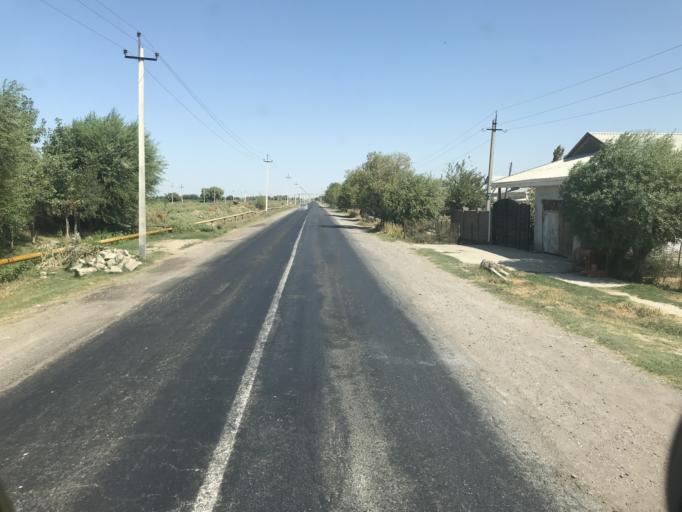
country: KZ
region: Ongtustik Qazaqstan
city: Ilyich
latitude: 40.8994
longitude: 68.4882
